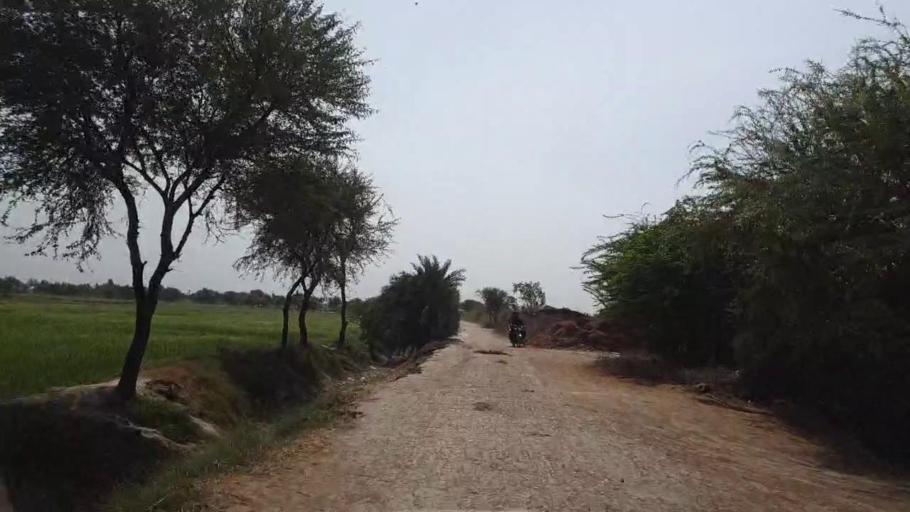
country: PK
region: Sindh
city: Matli
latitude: 25.0456
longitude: 68.6971
